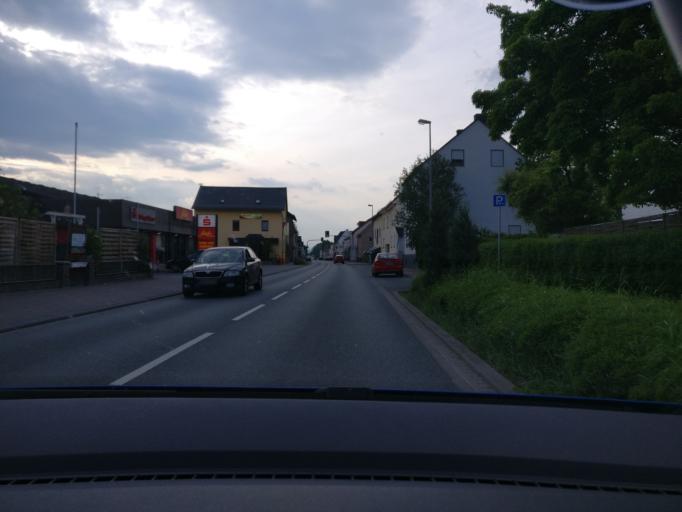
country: DE
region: Hesse
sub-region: Regierungsbezirk Giessen
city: Limburg an der Lahn
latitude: 50.3668
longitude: 8.0919
